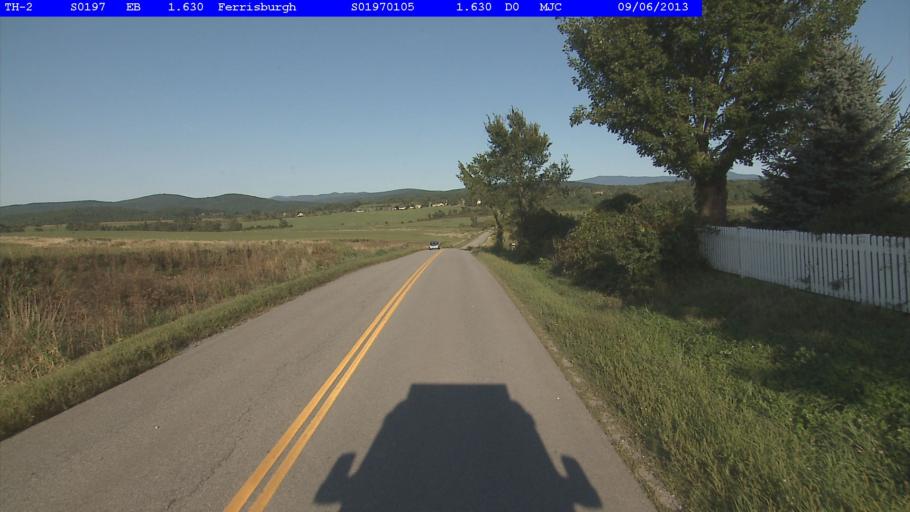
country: US
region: Vermont
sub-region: Addison County
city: Vergennes
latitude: 44.1755
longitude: -73.2073
